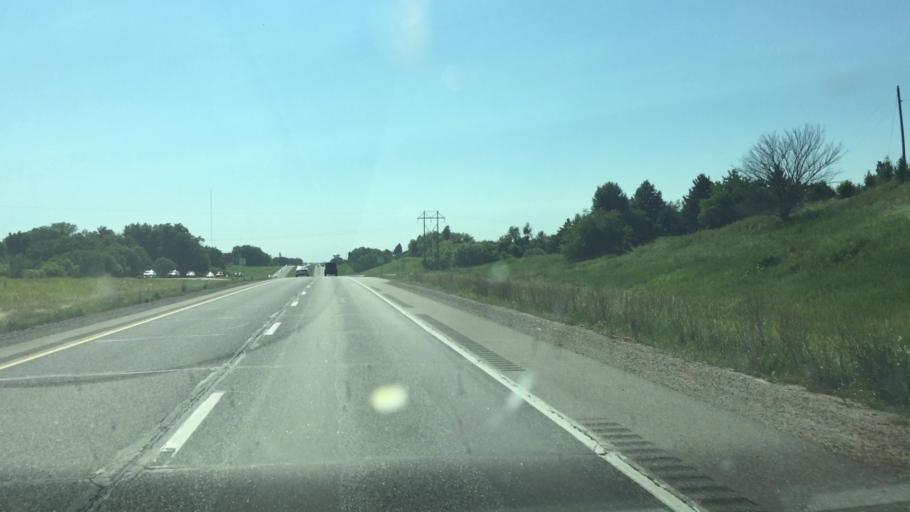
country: US
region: Iowa
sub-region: Linn County
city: Ely
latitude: 41.9260
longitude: -91.5918
